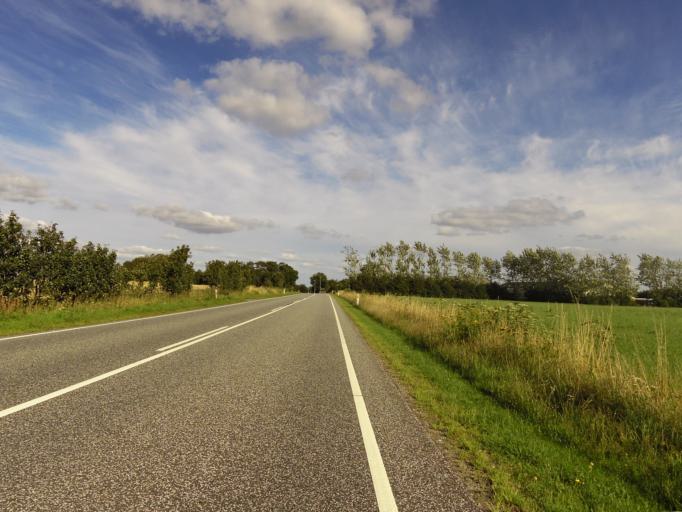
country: DK
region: South Denmark
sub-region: Haderslev Kommune
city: Gram
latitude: 55.2293
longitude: 8.9867
